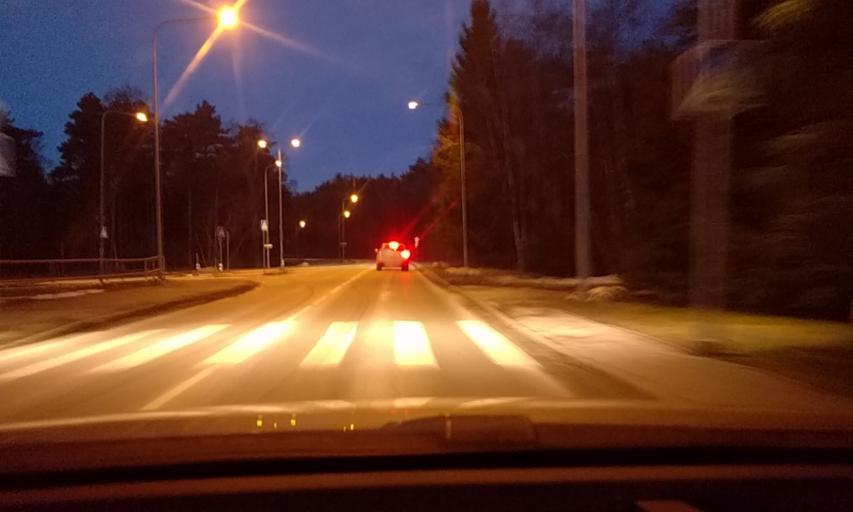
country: EE
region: Harju
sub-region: Viimsi vald
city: Viimsi
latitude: 59.4843
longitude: 24.8610
